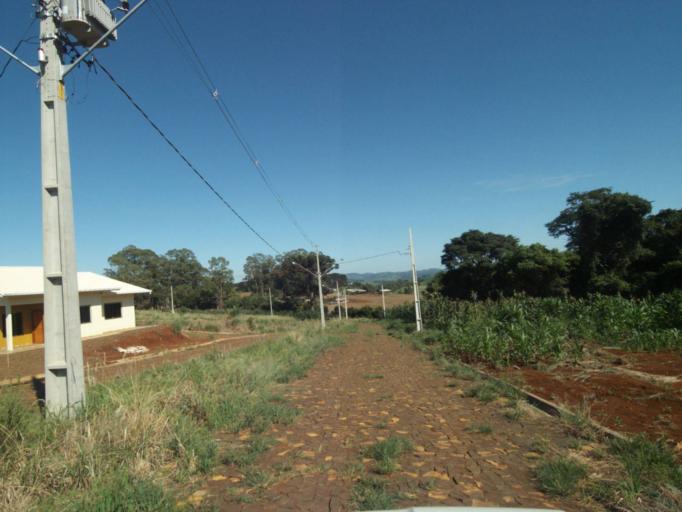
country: BR
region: Parana
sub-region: Laranjeiras Do Sul
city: Laranjeiras do Sul
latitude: -25.4851
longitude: -52.5260
